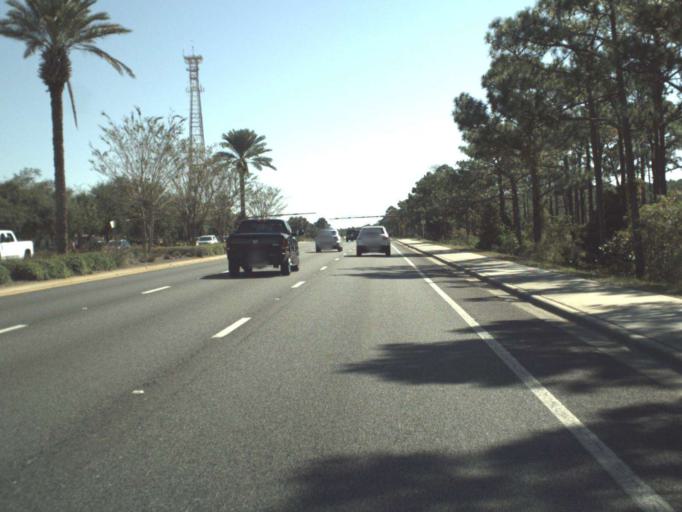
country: US
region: Florida
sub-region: Walton County
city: Miramar Beach
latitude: 30.3778
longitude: -86.3126
